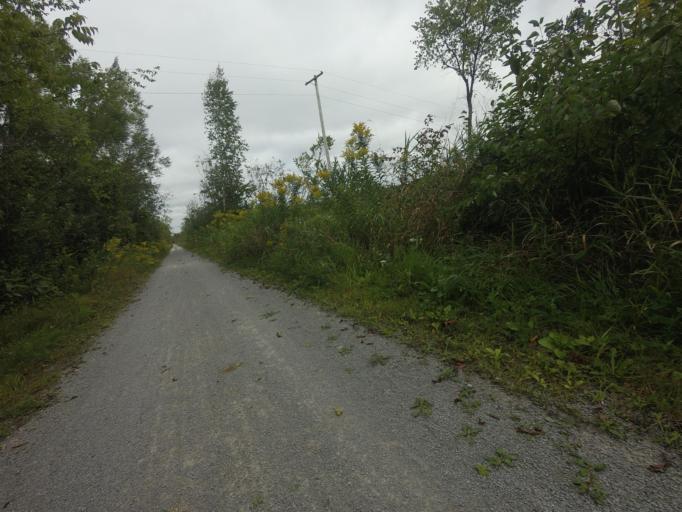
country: CA
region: Ontario
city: Uxbridge
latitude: 44.2390
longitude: -79.0458
